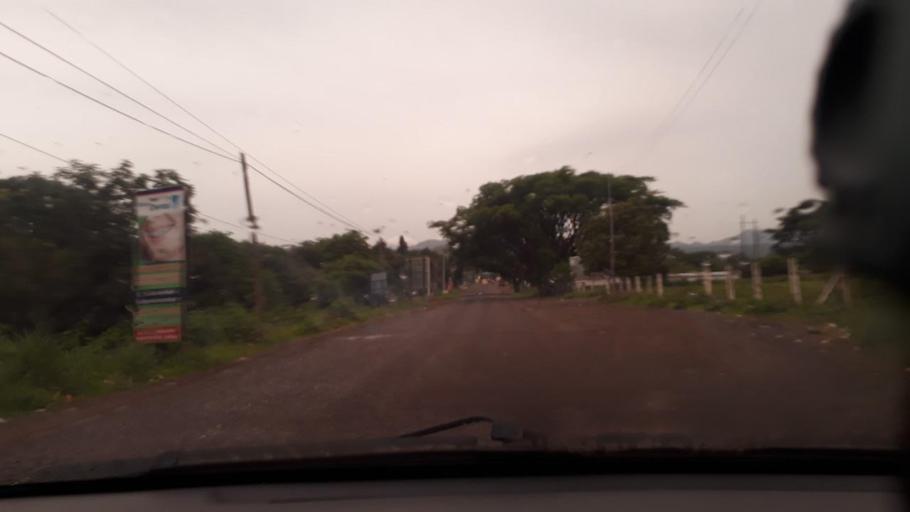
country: GT
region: Jutiapa
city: Asuncion Mita
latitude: 14.3035
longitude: -89.7175
